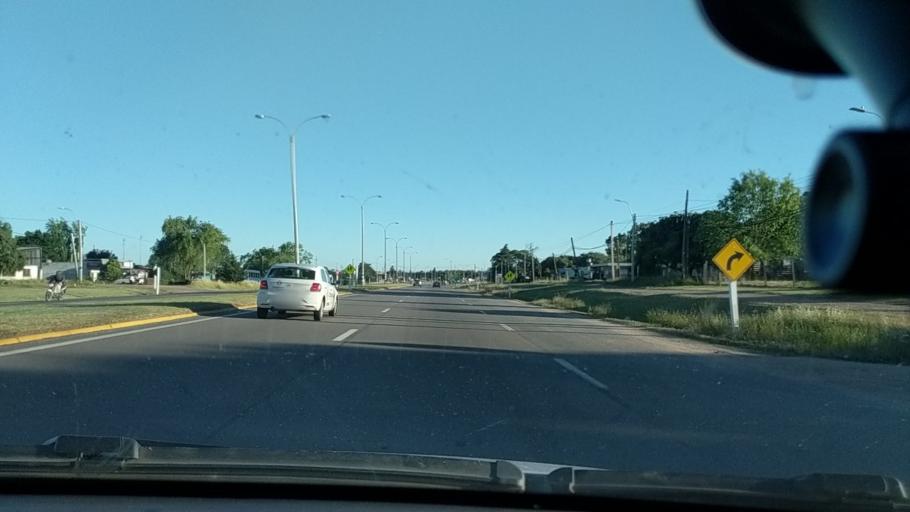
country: UY
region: Canelones
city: Progreso
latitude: -34.6437
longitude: -56.2441
